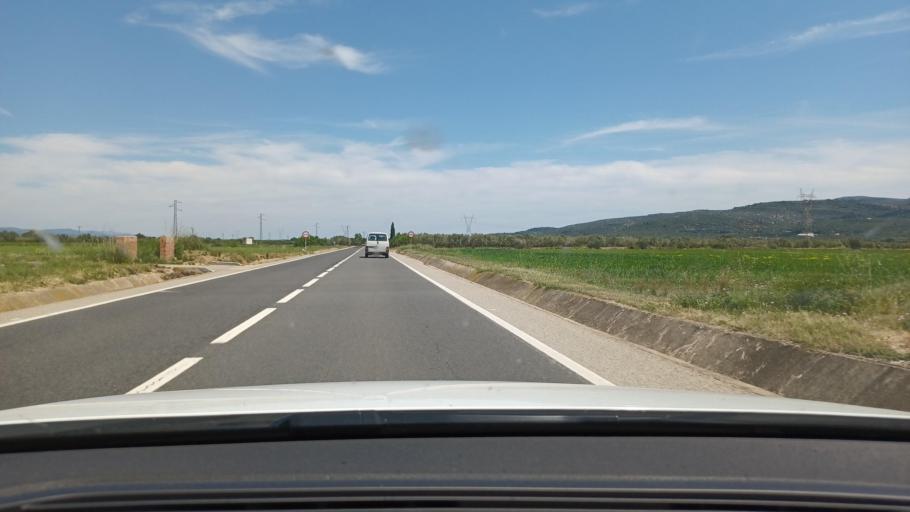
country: ES
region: Catalonia
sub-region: Provincia de Tarragona
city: Ulldecona
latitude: 40.6659
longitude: 0.4302
